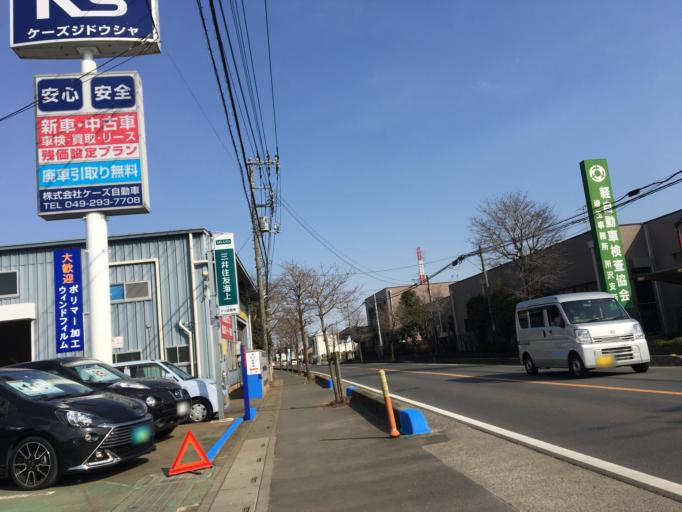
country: JP
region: Saitama
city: Oi
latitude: 35.8298
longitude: 139.5168
